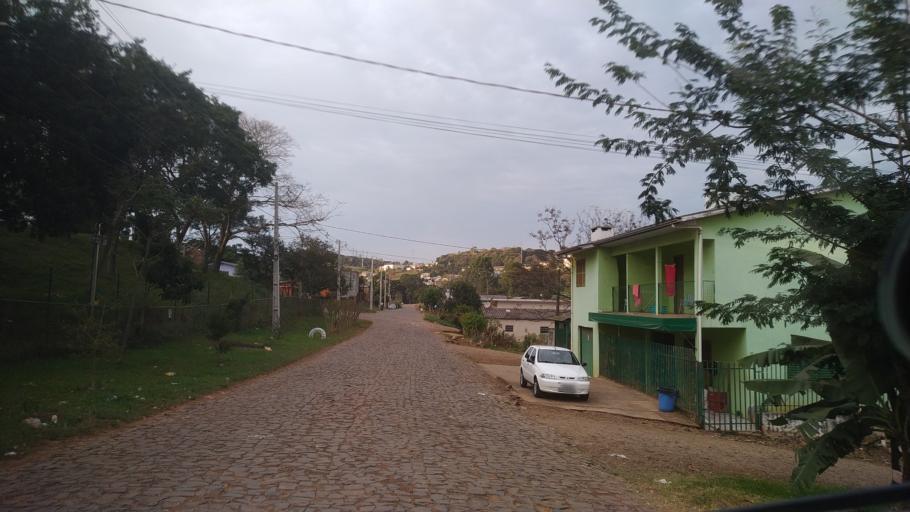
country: BR
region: Santa Catarina
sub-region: Chapeco
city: Chapeco
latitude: -27.1013
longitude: -52.5937
